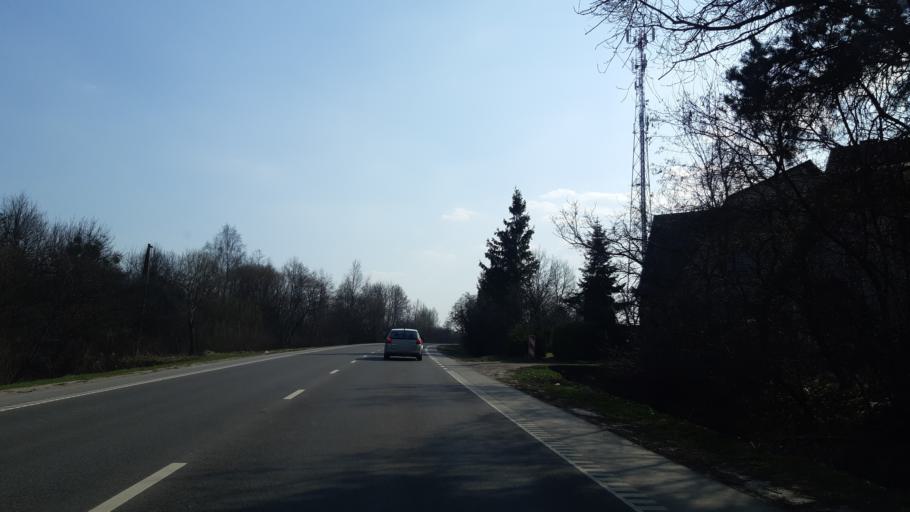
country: LT
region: Kauno apskritis
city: Dainava (Kaunas)
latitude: 54.8635
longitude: 23.9859
